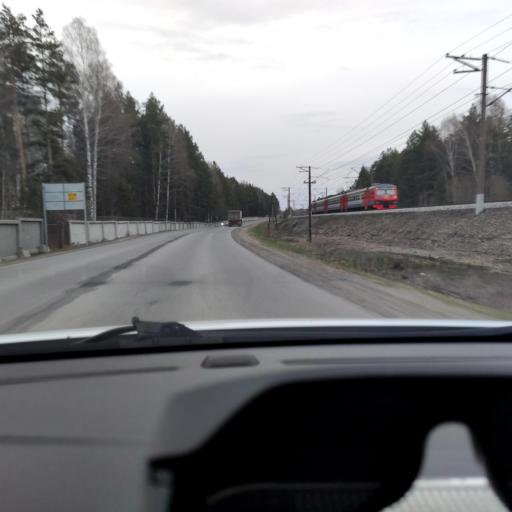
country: RU
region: Tatarstan
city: Vysokaya Gora
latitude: 55.8945
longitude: 49.2528
